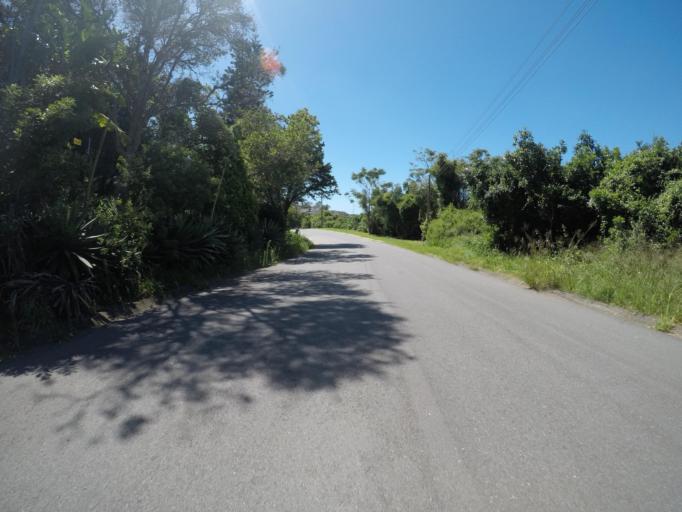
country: ZA
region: Eastern Cape
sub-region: Buffalo City Metropolitan Municipality
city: East London
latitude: -32.9724
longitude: 27.9460
